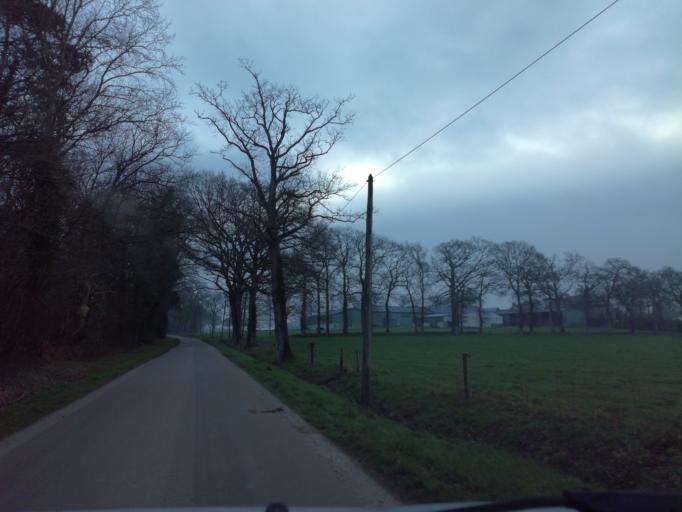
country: FR
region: Brittany
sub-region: Departement d'Ille-et-Vilaine
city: Gosne
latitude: 48.2624
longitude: -1.4718
